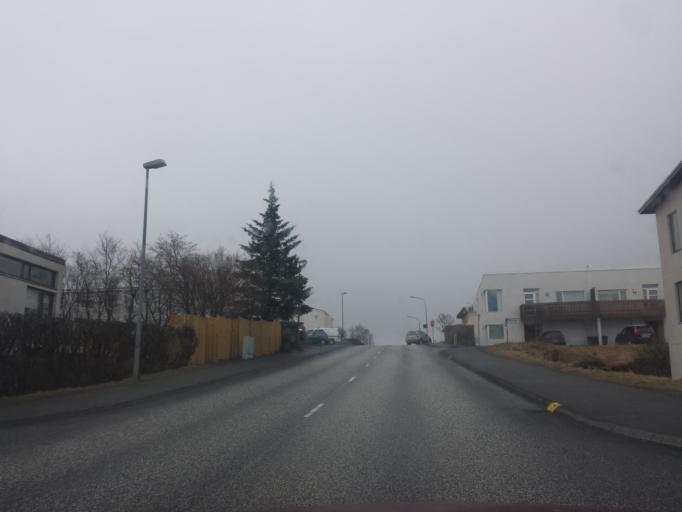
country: IS
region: Capital Region
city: Reykjavik
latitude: 64.1120
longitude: -21.8676
